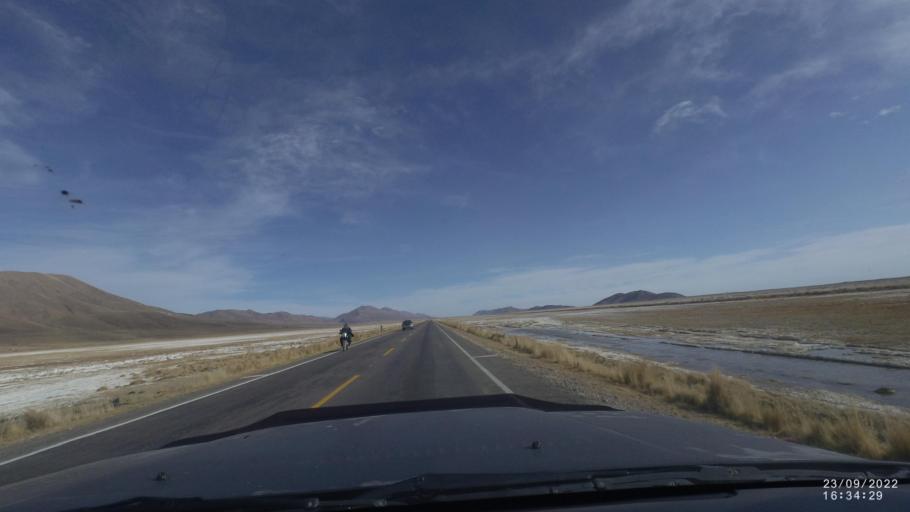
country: BO
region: Oruro
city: Machacamarca
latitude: -18.1898
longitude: -67.0141
